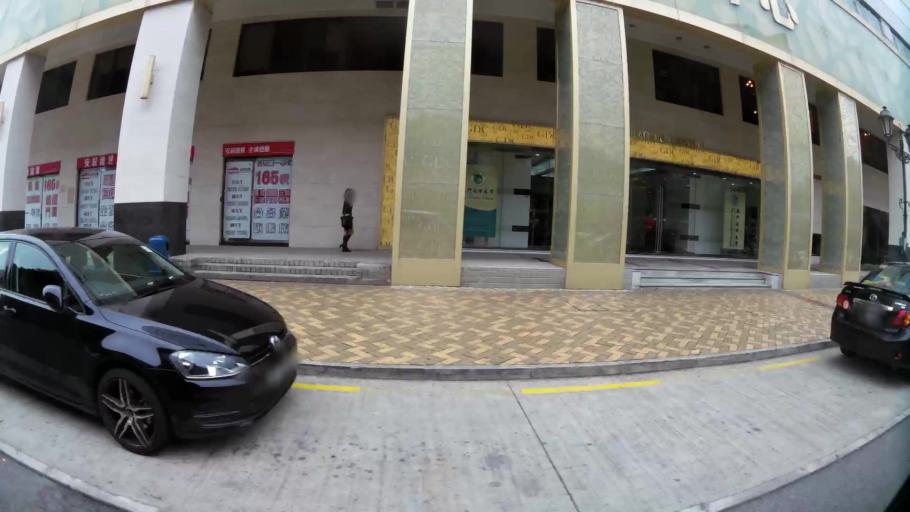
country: MO
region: Macau
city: Macau
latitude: 22.1887
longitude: 113.5543
